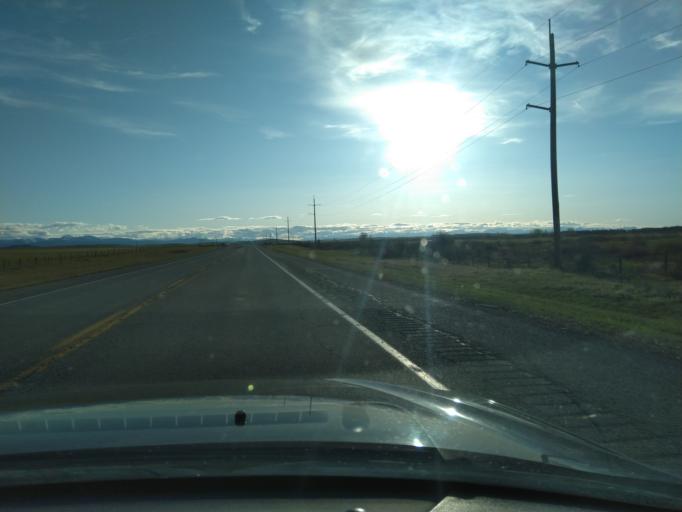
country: CA
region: Alberta
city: Cochrane
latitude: 51.0233
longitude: -114.4118
